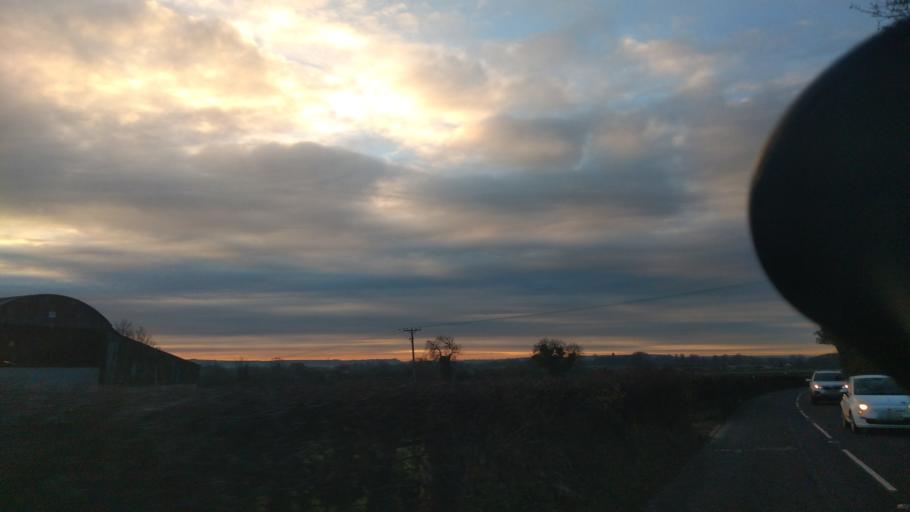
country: GB
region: England
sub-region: Wiltshire
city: Bradford-on-Avon
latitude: 51.3341
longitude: -2.2553
